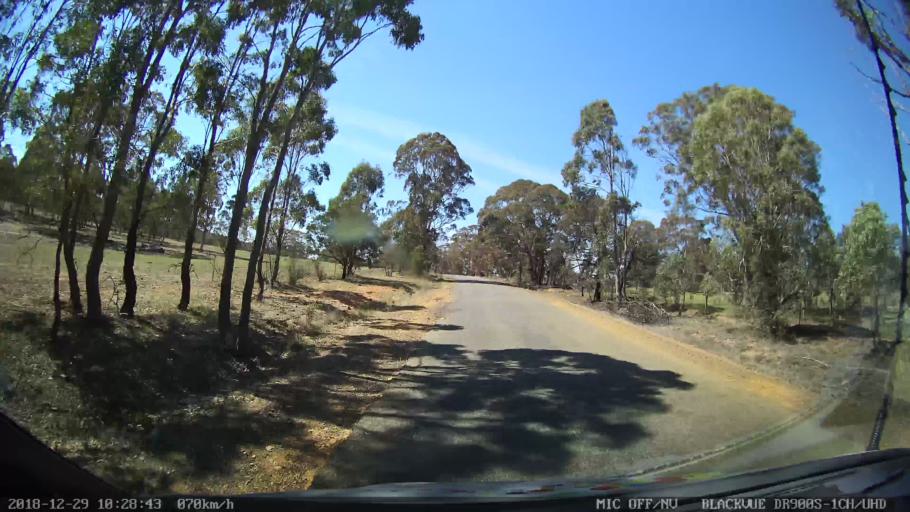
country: AU
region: New South Wales
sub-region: Yass Valley
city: Gundaroo
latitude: -34.9450
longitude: 149.4551
